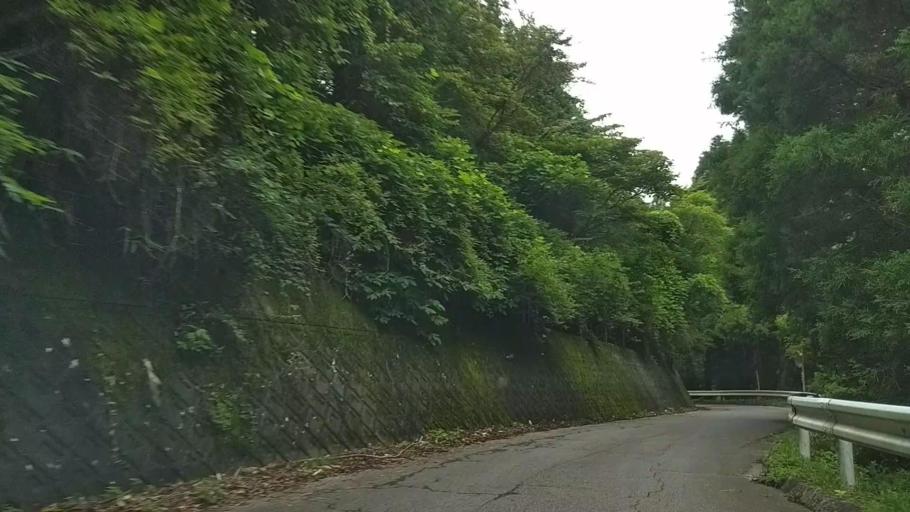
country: JP
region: Shizuoka
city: Gotemba
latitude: 35.3219
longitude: 139.0087
